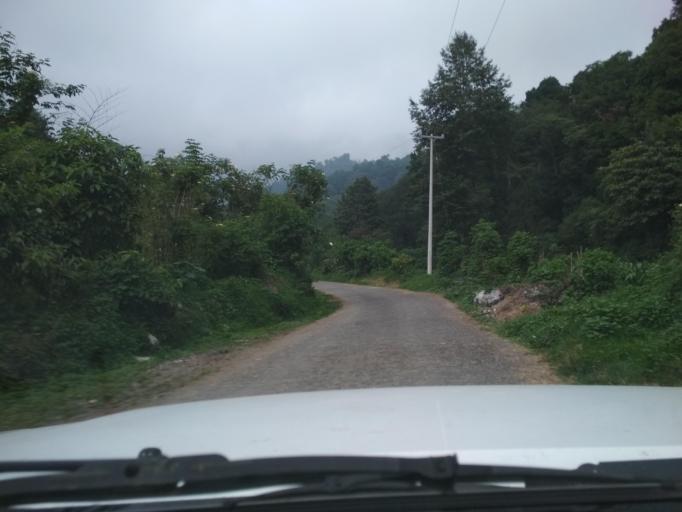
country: MX
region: Veracruz
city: La Perla
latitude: 18.9298
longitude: -97.1436
